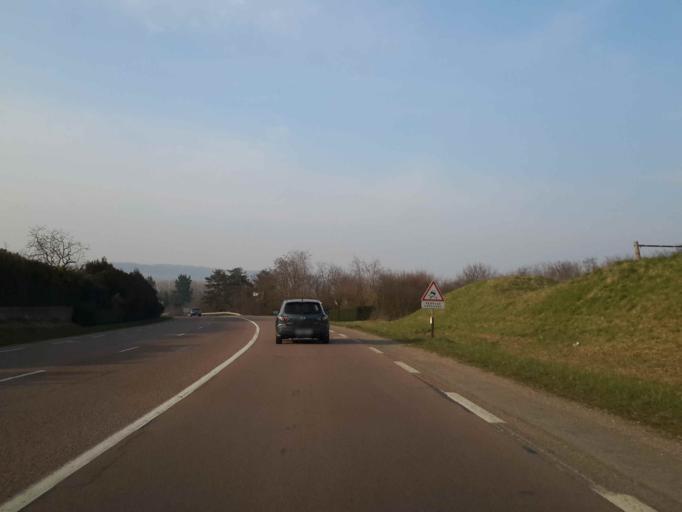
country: FR
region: Bourgogne
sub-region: Departement de Saone-et-Loire
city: Chagny
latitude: 46.9098
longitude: 4.7592
